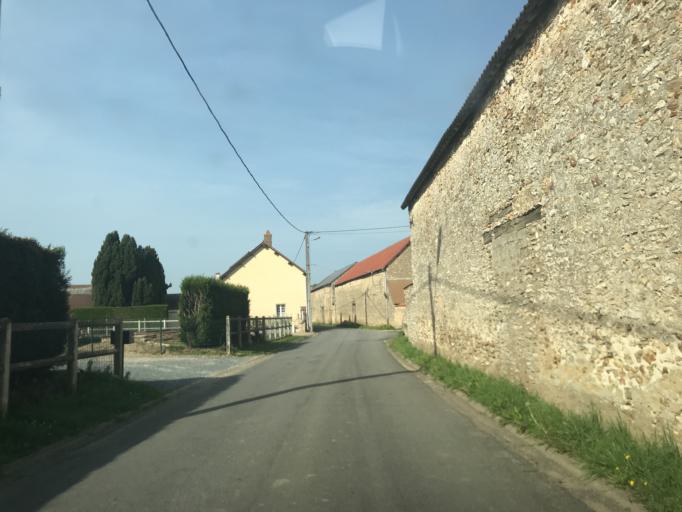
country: FR
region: Haute-Normandie
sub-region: Departement de l'Eure
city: La Chapelle-Reanville
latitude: 49.0603
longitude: 1.4148
